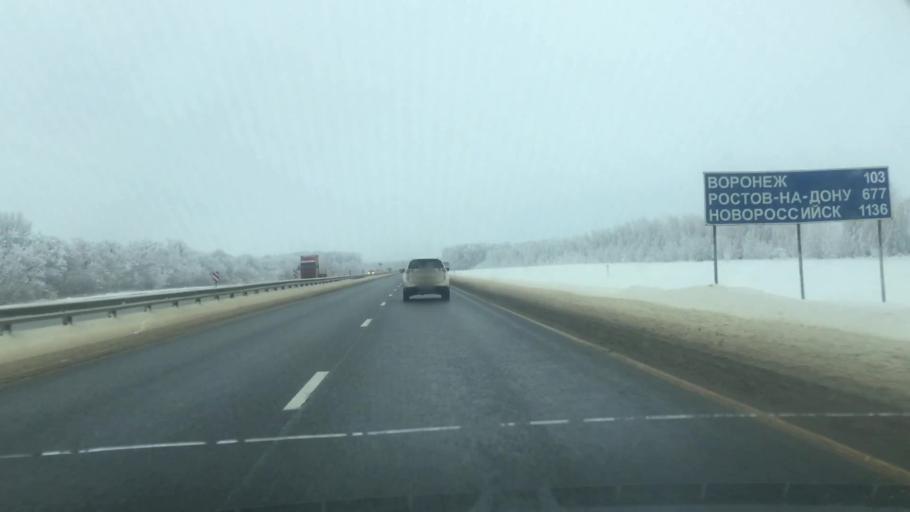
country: RU
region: Lipetsk
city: Zadonsk
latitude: 52.4985
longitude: 38.7554
